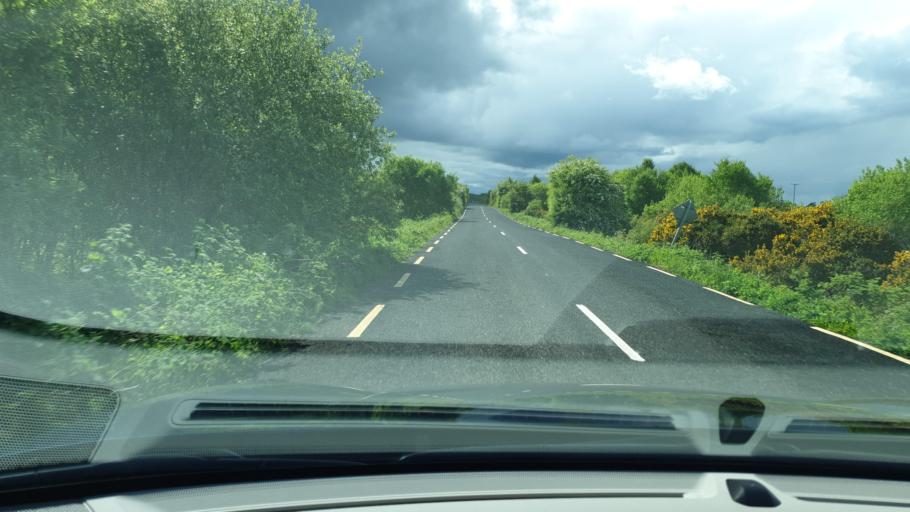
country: IE
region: Leinster
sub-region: Uibh Fhaili
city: Clara
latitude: 53.2378
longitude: -7.6898
